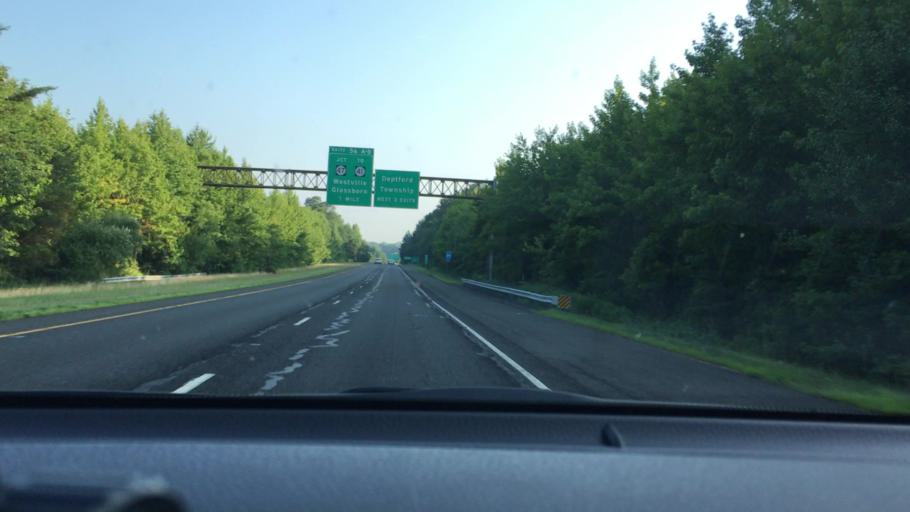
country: US
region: New Jersey
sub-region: Gloucester County
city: Wenonah
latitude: 39.7802
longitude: -75.1155
